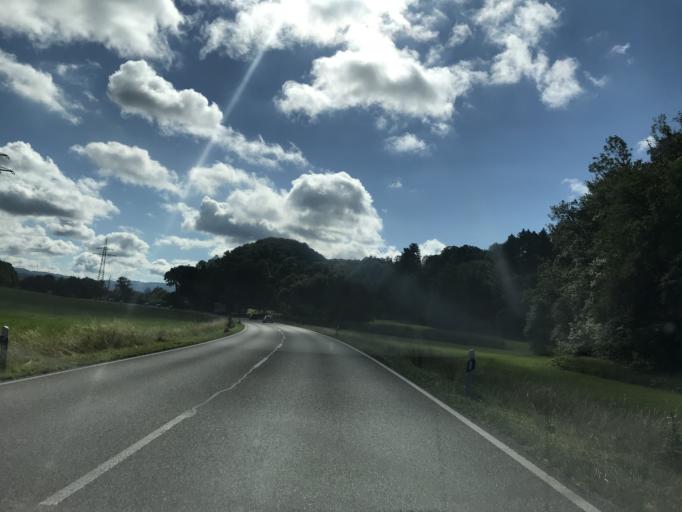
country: DE
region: Baden-Wuerttemberg
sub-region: Freiburg Region
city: Steinen
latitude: 47.6369
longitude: 7.7326
